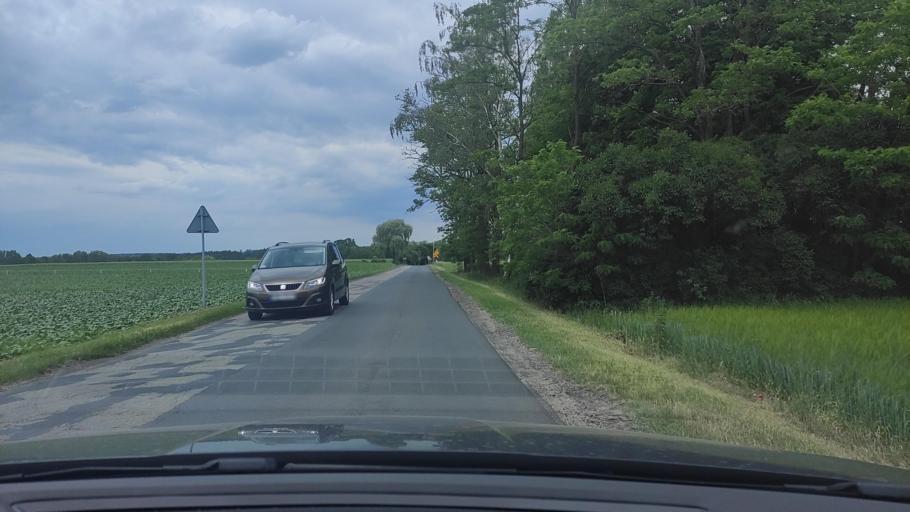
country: PL
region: Greater Poland Voivodeship
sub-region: Powiat poznanski
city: Kostrzyn
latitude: 52.4438
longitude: 17.1697
